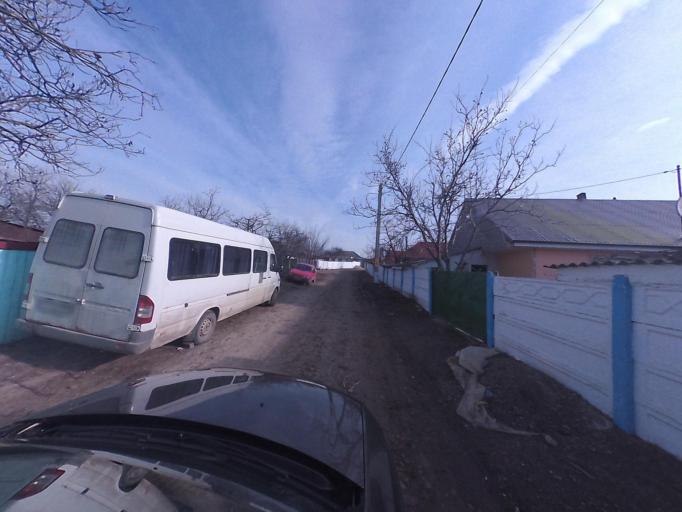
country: RO
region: Vaslui
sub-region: Comuna Solesti
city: Solesti
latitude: 46.8054
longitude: 27.7858
